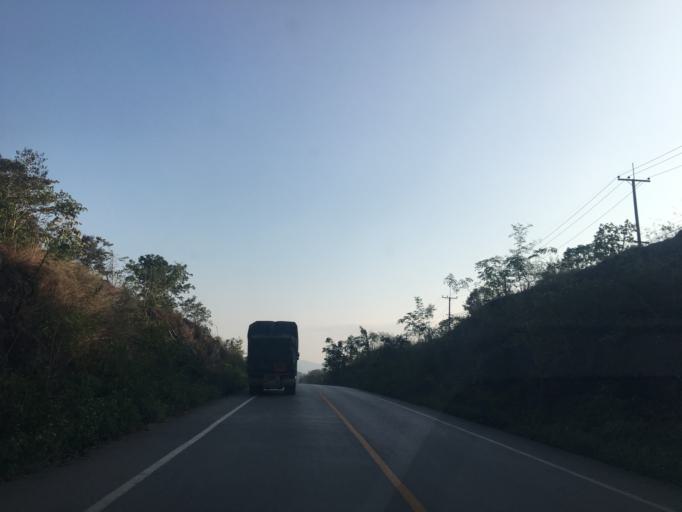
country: TH
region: Lampang
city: Ngao
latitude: 18.6509
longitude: 100.0177
